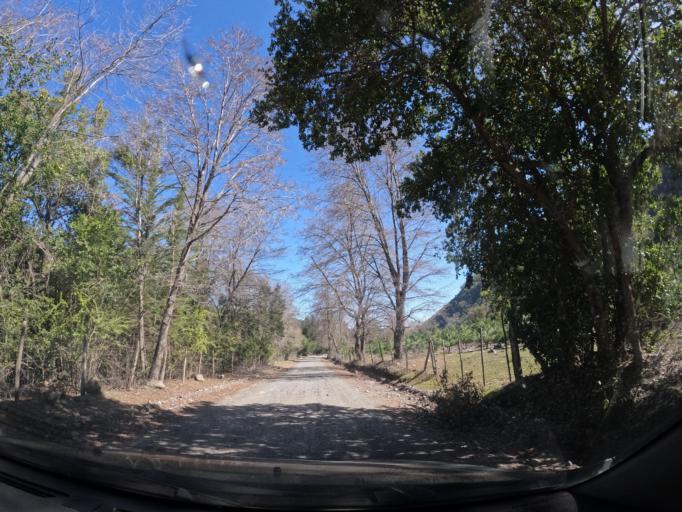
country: CL
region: Maule
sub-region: Provincia de Linares
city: Longavi
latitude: -36.2276
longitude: -71.3919
